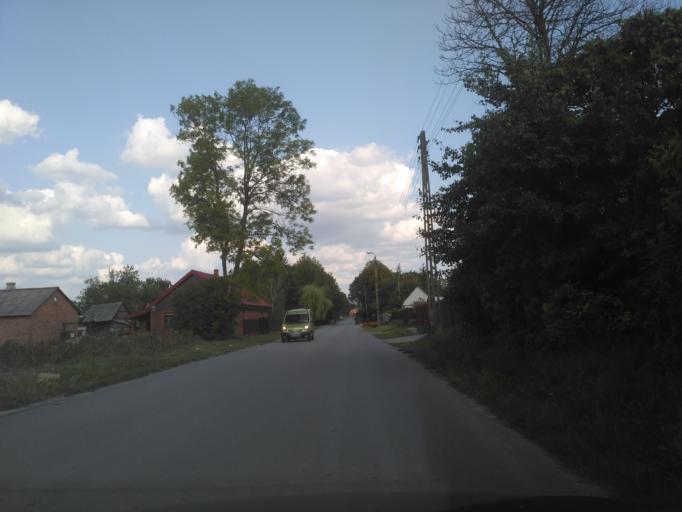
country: PL
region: Lublin Voivodeship
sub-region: Powiat chelmski
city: Pokrowka
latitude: 51.0685
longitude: 23.4971
